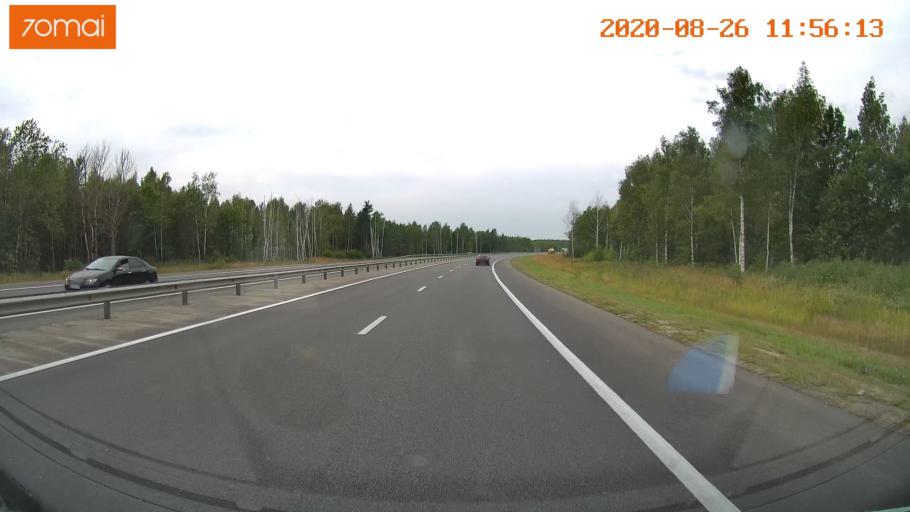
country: RU
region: Rjazan
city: Kiritsy
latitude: 54.2637
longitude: 40.3824
